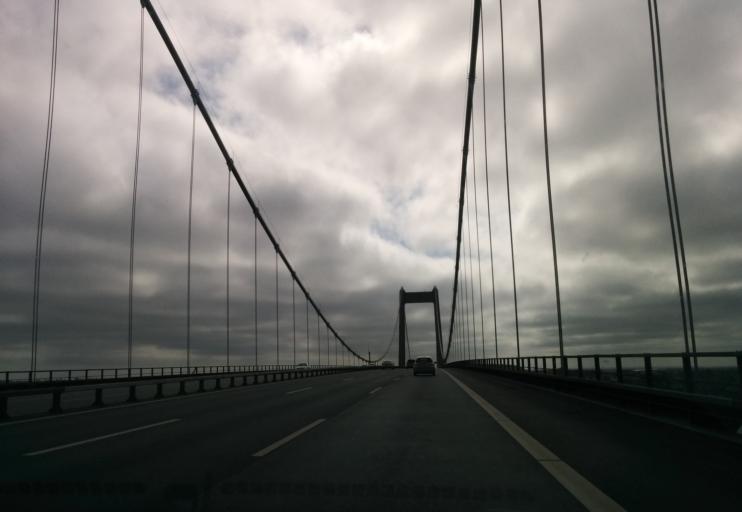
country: DK
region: South Denmark
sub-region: Middelfart Kommune
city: Middelfart
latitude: 55.5193
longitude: 9.7456
